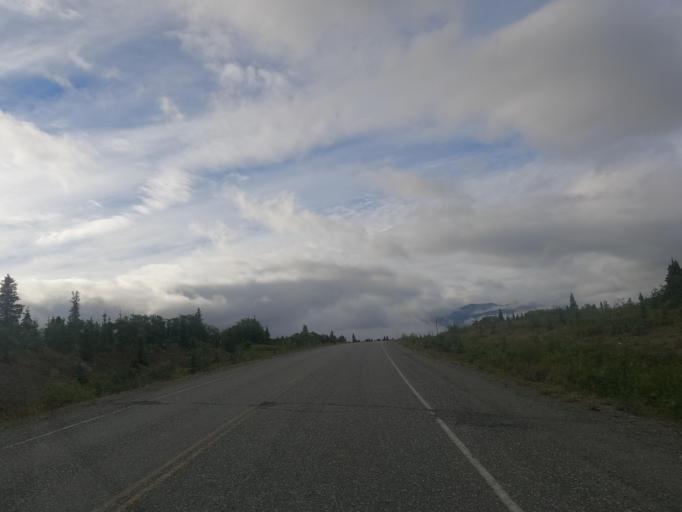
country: CA
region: Yukon
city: Haines Junction
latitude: 59.9439
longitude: -136.8005
